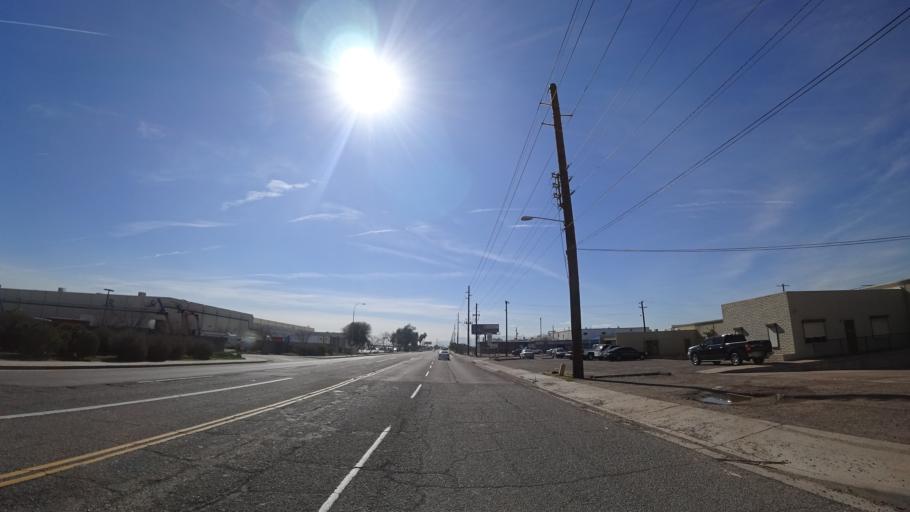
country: US
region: Arizona
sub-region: Maricopa County
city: Tolleson
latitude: 33.4509
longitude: -112.1867
